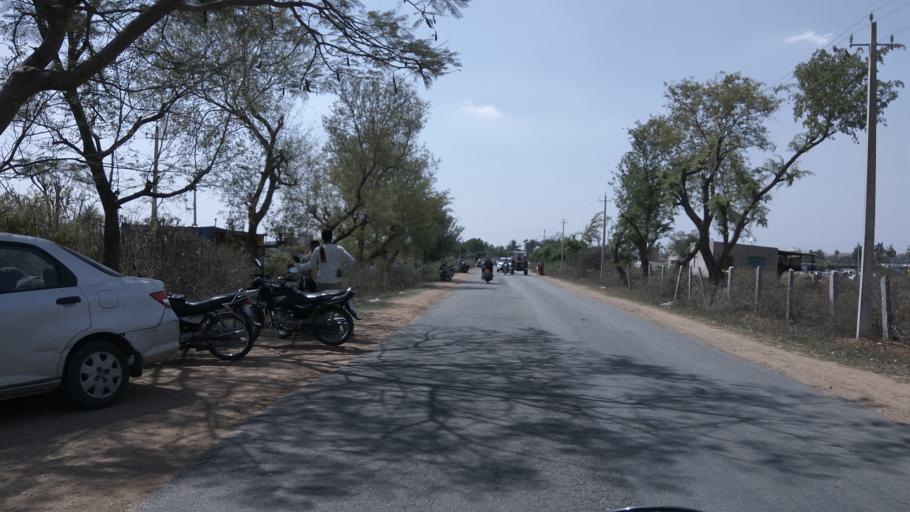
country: IN
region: Karnataka
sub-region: Kolar
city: Mulbagal
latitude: 13.1662
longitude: 78.3672
